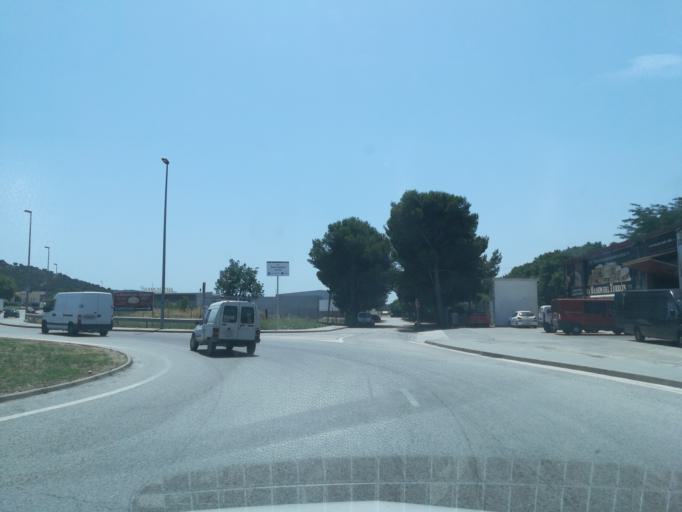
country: ES
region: Catalonia
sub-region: Provincia de Girona
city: la Jonquera
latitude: 42.4134
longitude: 2.8737
